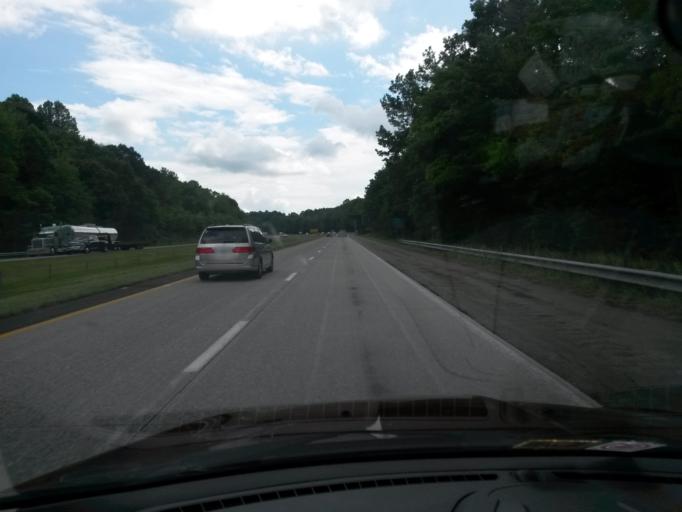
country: US
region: Virginia
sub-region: Carroll County
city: Cana
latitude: 36.5419
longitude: -80.7488
